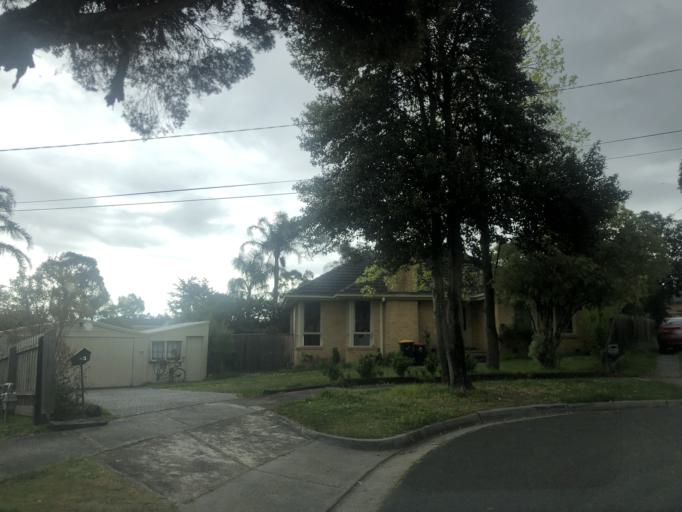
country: AU
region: Victoria
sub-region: Greater Dandenong
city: Dandenong North
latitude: -37.9659
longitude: 145.2206
